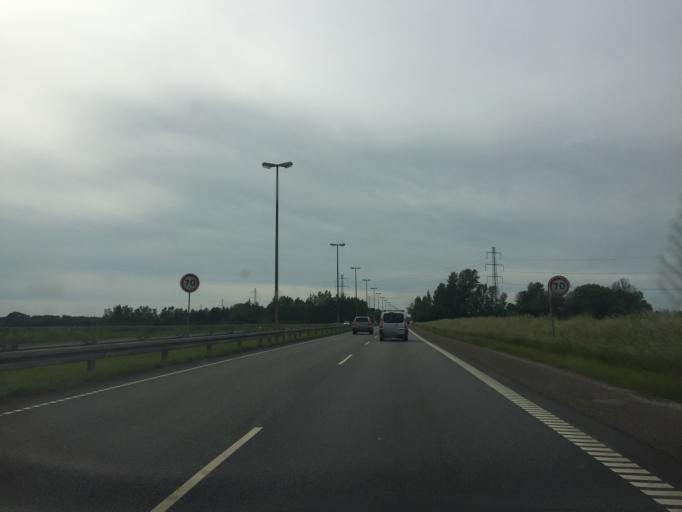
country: DK
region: Capital Region
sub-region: Hoje-Taastrup Kommune
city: Taastrup
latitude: 55.6295
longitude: 12.3005
